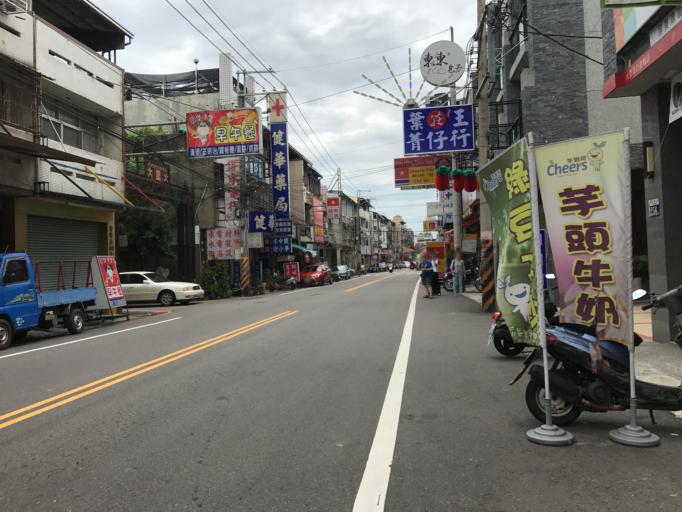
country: TW
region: Taiwan
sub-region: Taichung City
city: Taichung
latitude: 24.0871
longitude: 120.7075
